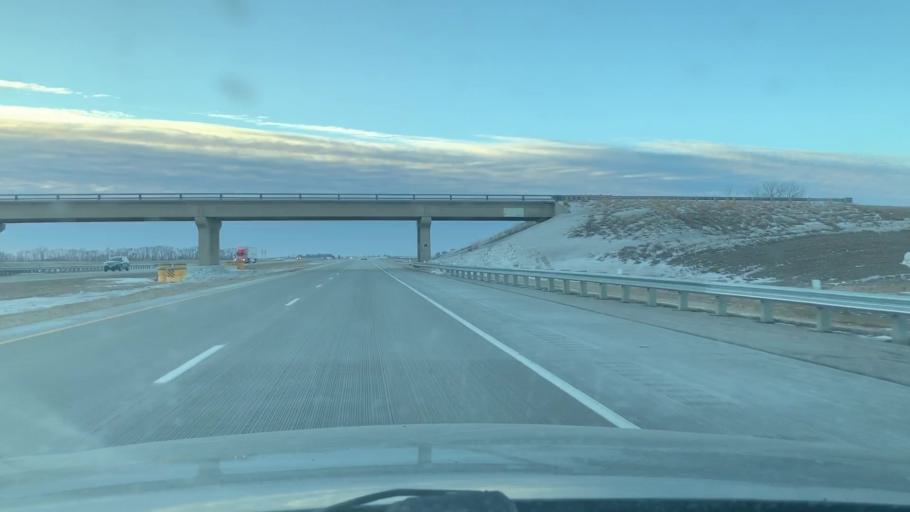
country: US
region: North Dakota
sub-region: Cass County
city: Casselton
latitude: 46.8758
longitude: -97.4921
